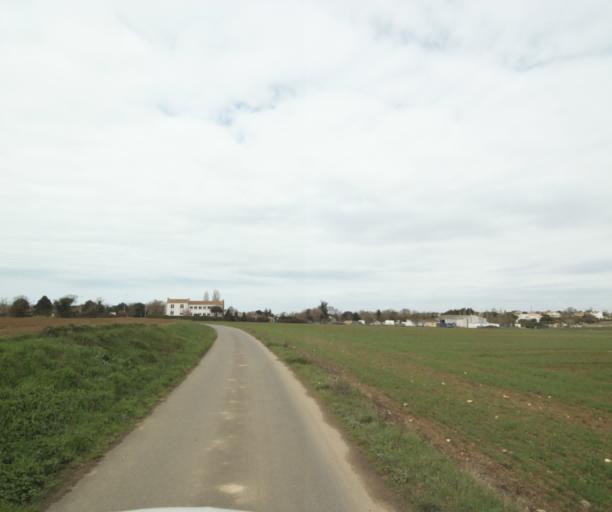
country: FR
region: Poitou-Charentes
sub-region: Departement de la Charente-Maritime
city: Nieul-sur-Mer
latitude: 46.1885
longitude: -1.1789
